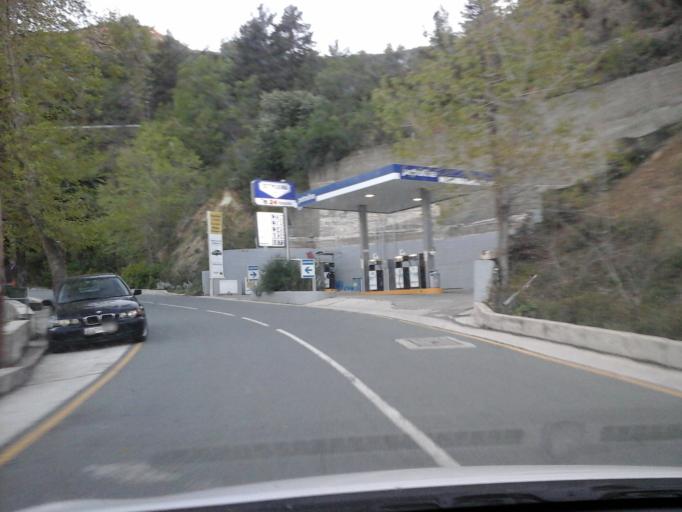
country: CY
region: Lefkosia
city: Kakopetria
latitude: 34.9704
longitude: 32.8262
